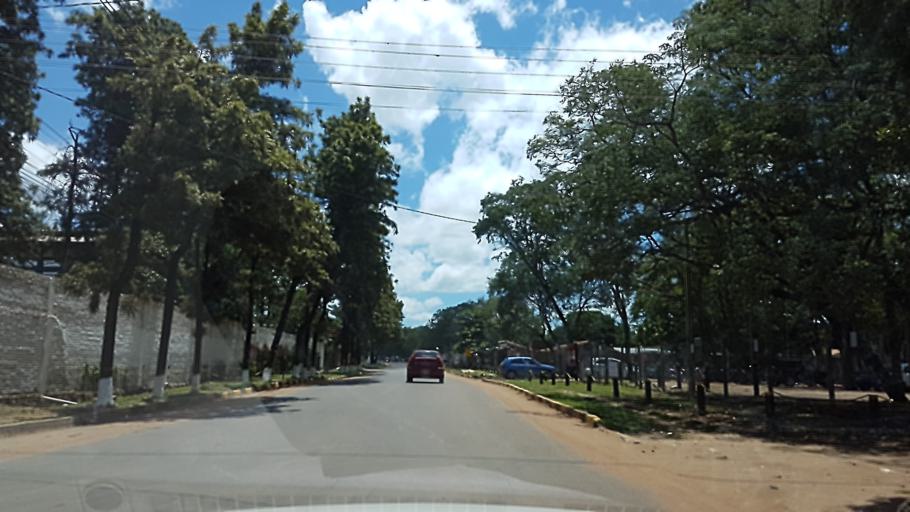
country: PY
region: Central
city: Colonia Mariano Roque Alonso
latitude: -25.2347
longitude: -57.5273
